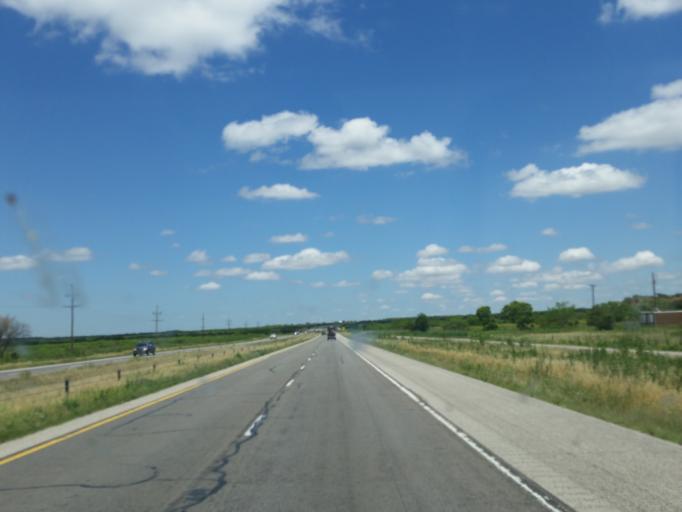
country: US
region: Texas
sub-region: Nolan County
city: Sweetwater
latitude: 32.4946
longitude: -100.2889
